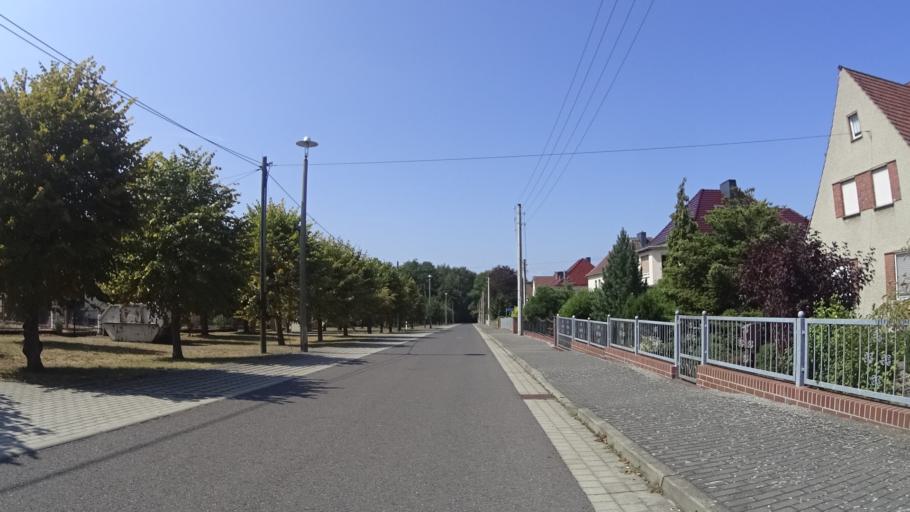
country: DE
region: Brandenburg
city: Tschernitz
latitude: 51.6020
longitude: 14.5855
